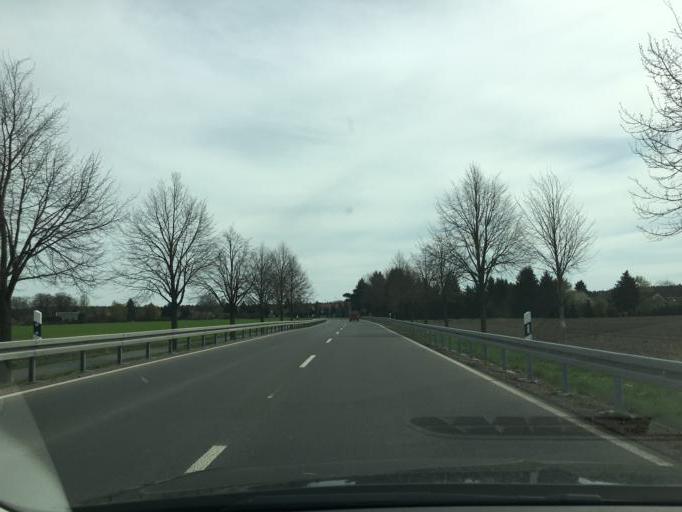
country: DE
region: Saxony
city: Schleife
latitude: 51.5732
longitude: 14.4905
